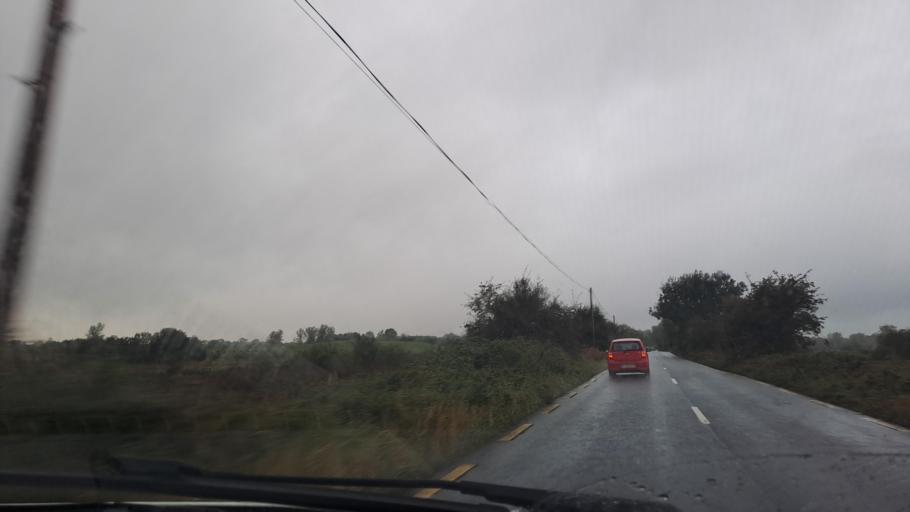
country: GB
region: Northern Ireland
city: Crossmaglen
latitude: 53.9707
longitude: -6.5859
